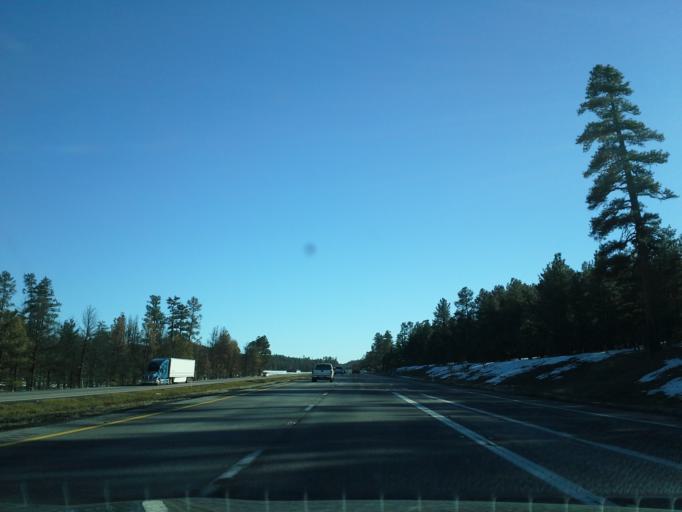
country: US
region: Arizona
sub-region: Coconino County
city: Mountainaire
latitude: 35.0148
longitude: -111.6849
